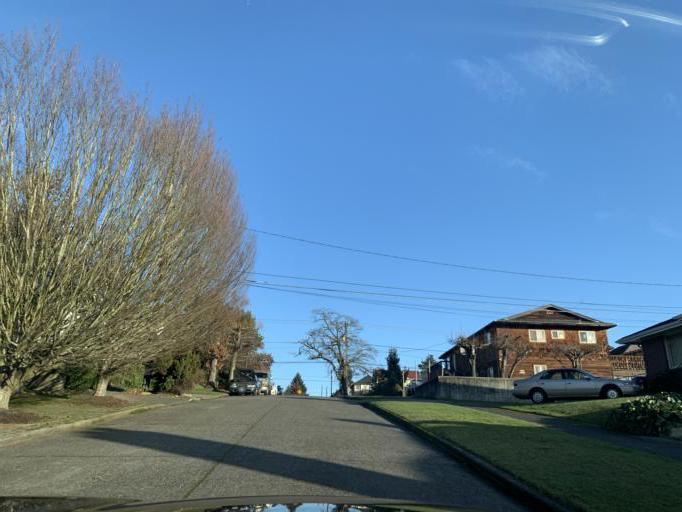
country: US
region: Washington
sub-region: King County
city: Seattle
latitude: 47.5760
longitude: -122.3158
